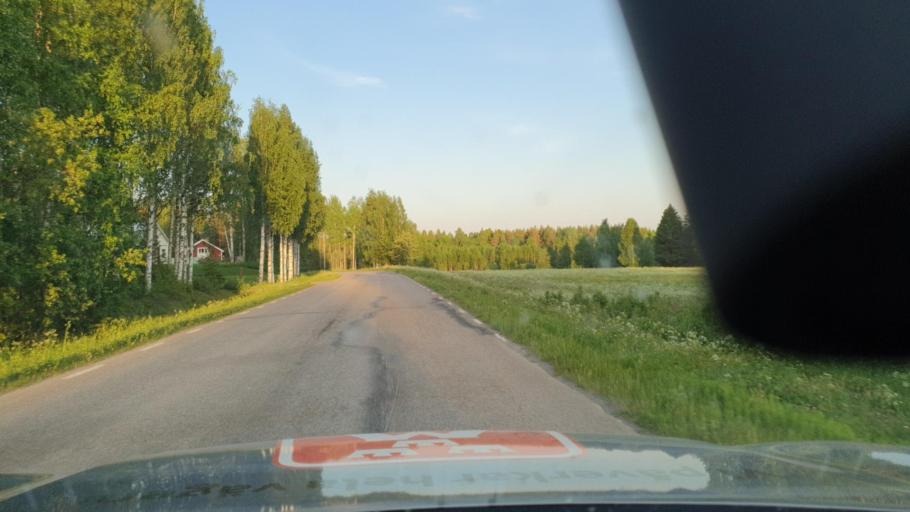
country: SE
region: Norrbotten
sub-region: Bodens Kommun
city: Boden
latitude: 66.0459
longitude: 21.7899
